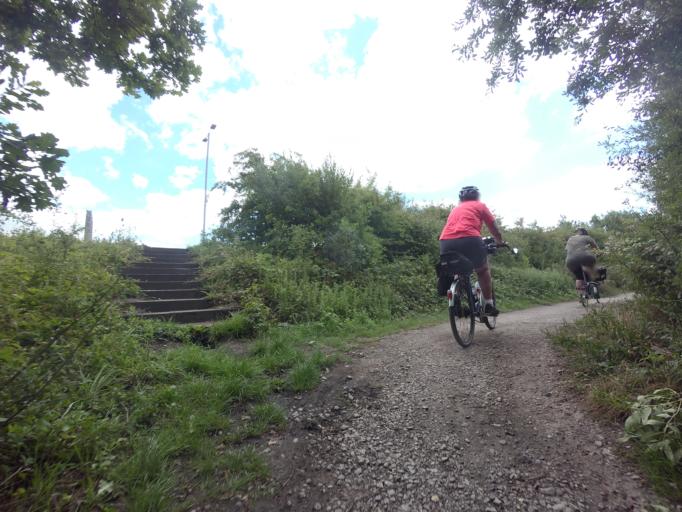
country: GB
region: England
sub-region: East Sussex
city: Hailsham
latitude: 50.8321
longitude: 0.2383
